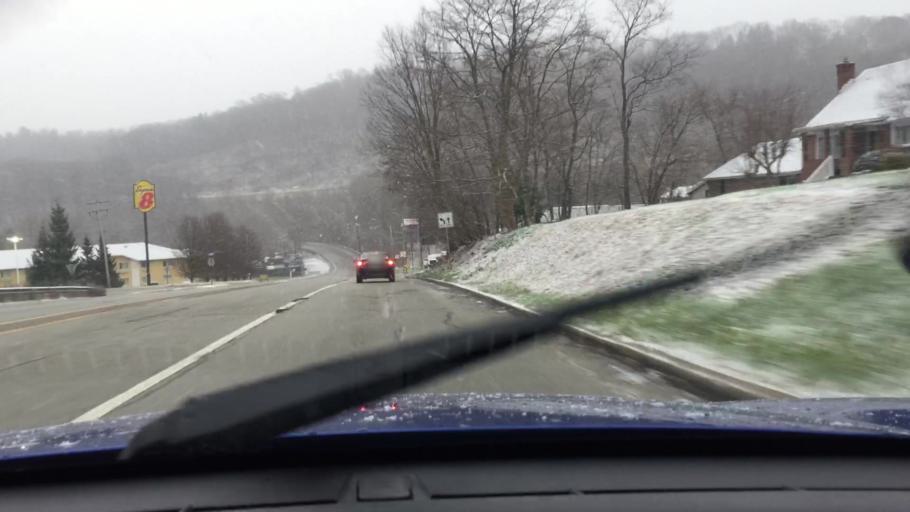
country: US
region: Pennsylvania
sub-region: Washington County
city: Canonsburg
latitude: 40.2661
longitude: -80.1673
